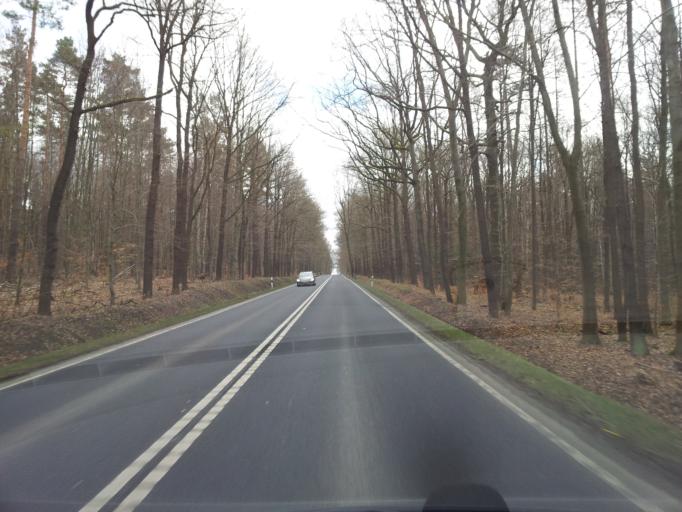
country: DE
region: Saxony
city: Laussnitz
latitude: 51.2414
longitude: 13.8604
